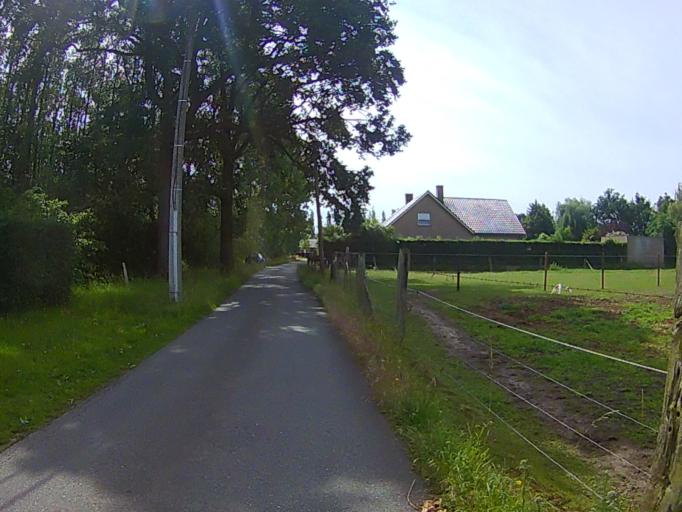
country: BE
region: Flanders
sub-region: Provincie Antwerpen
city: Putte
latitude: 51.0612
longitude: 4.6440
